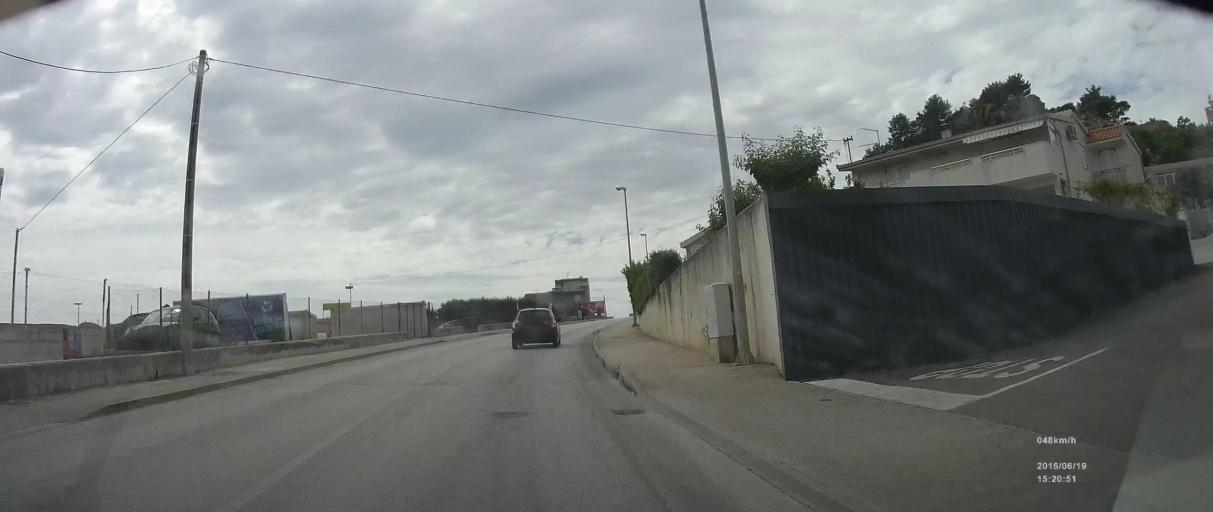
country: HR
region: Splitsko-Dalmatinska
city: Kamen
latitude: 43.5071
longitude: 16.5065
